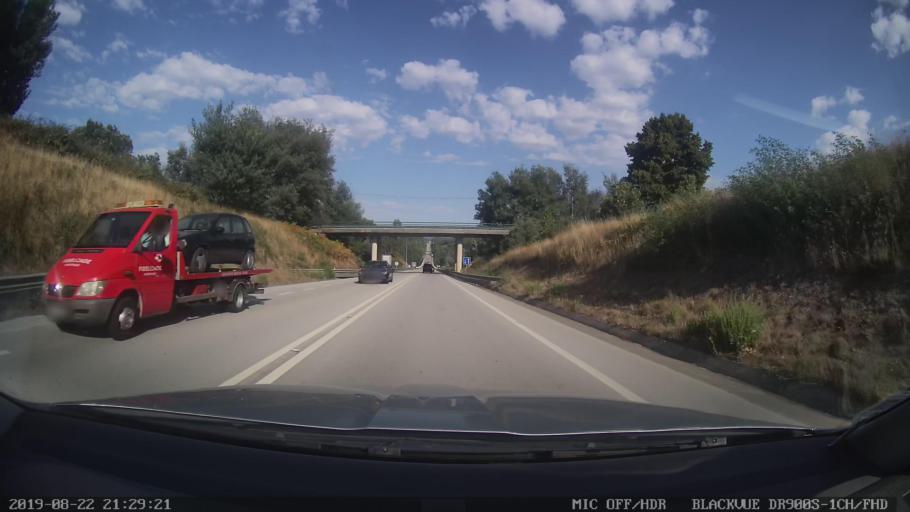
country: PT
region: Leiria
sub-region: Pedrogao Grande
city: Pedrogao Grande
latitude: 39.9017
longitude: -8.1340
